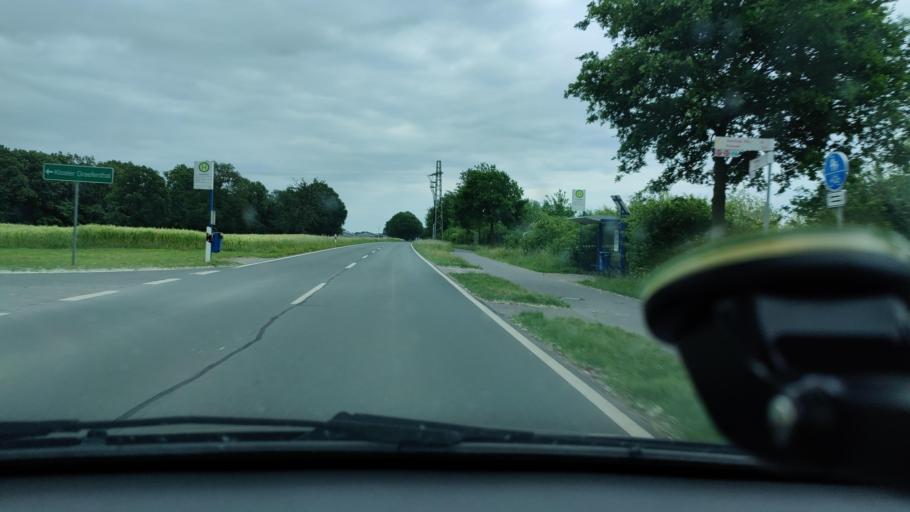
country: DE
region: North Rhine-Westphalia
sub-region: Regierungsbezirk Dusseldorf
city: Goch
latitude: 51.7028
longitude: 6.1062
